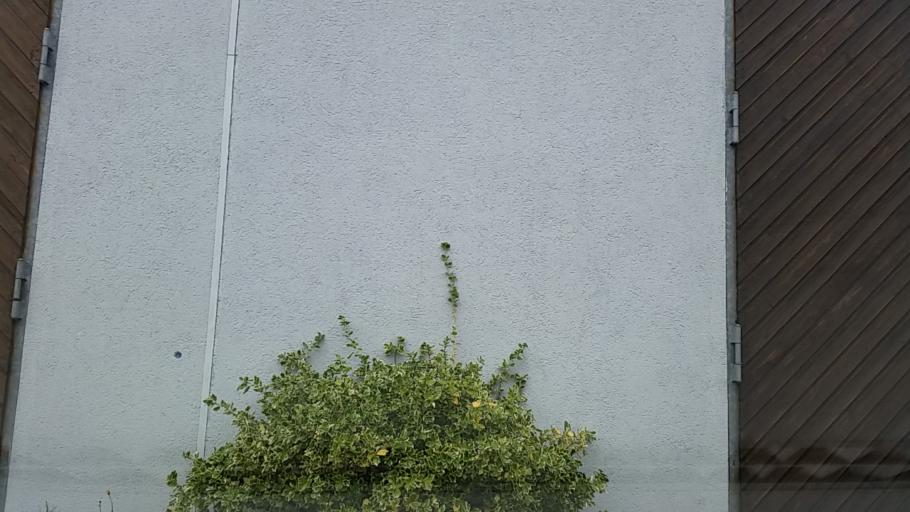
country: DE
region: Bavaria
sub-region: Regierungsbezirk Unterfranken
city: Himmelstadt
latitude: 49.9259
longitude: 9.8077
